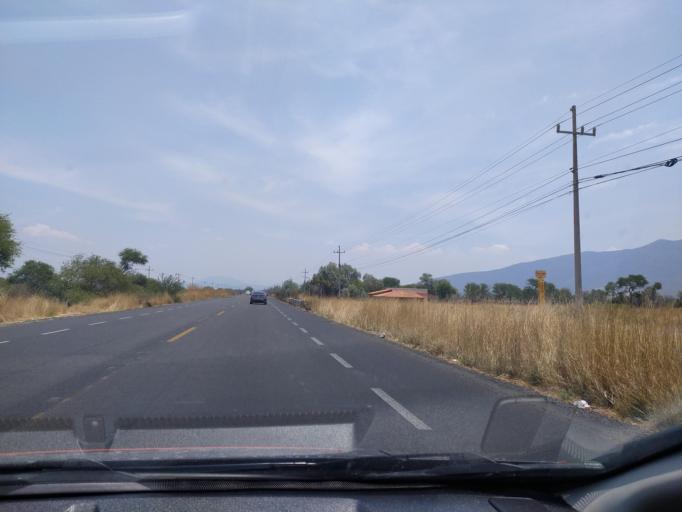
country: MX
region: Jalisco
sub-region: Zacoalco de Torres
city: Barranca de Otates (Barranca de Otatan)
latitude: 20.3205
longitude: -103.5901
